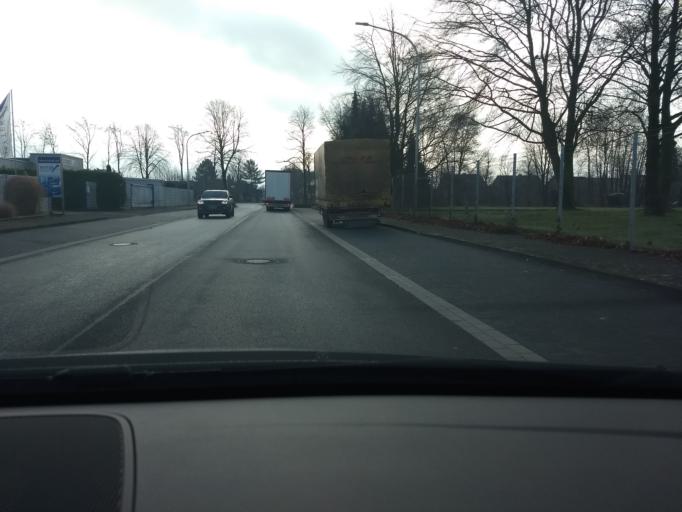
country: DE
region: North Rhine-Westphalia
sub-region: Regierungsbezirk Munster
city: Borken
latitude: 51.8501
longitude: 6.8785
